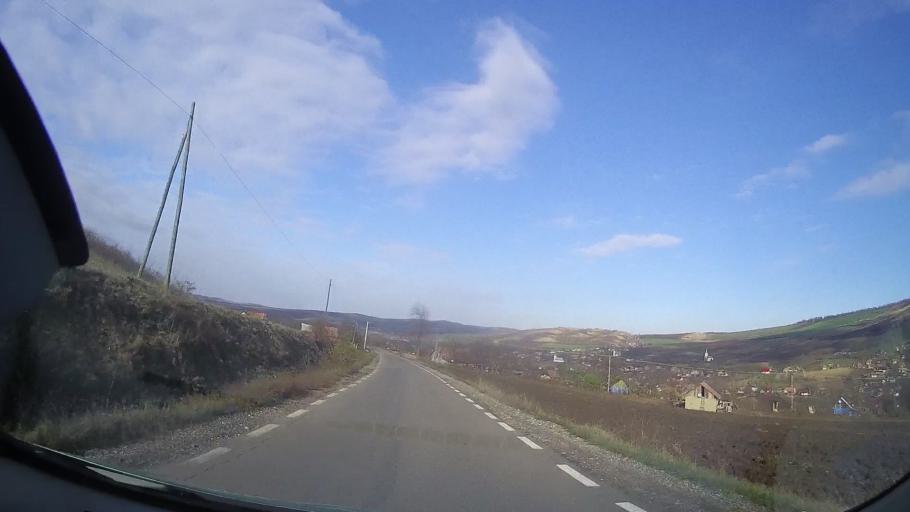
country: RO
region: Mures
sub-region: Comuna Sanger
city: Sanger
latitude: 46.5499
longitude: 24.1454
